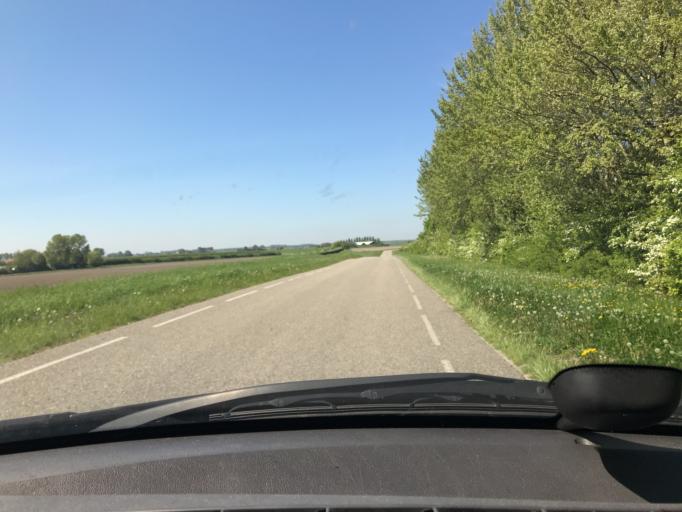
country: NL
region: Zeeland
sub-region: Gemeente Goes
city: Goes
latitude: 51.5395
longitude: 3.7983
